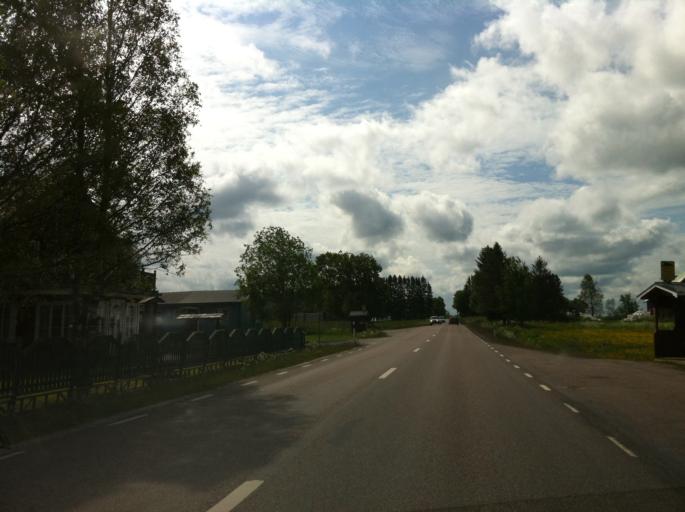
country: SE
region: Vaermland
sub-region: Sunne Kommun
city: Sunne
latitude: 59.6680
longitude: 13.1519
